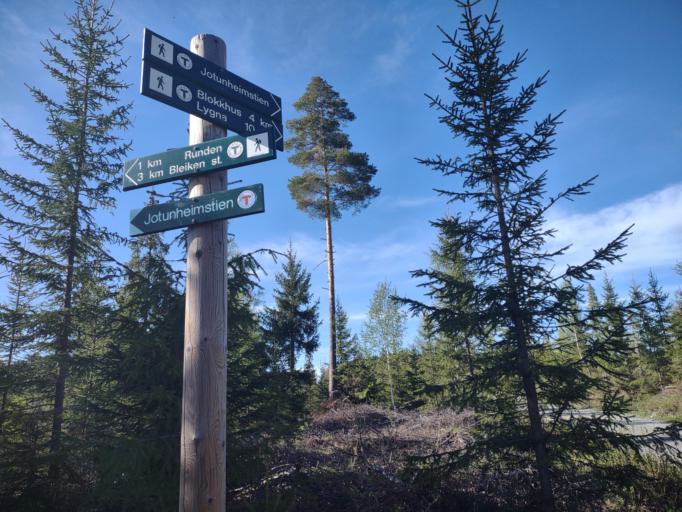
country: NO
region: Oppland
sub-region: Gran
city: Jaren
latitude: 60.4698
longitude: 10.5369
